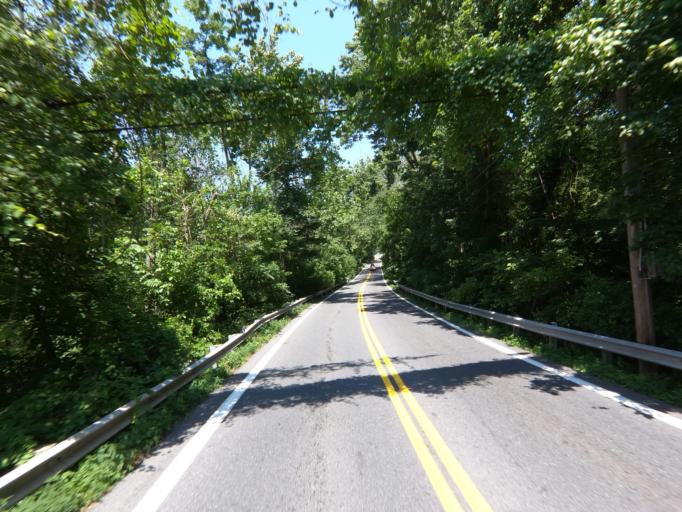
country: US
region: Maryland
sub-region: Frederick County
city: Green Valley
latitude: 39.2779
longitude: -77.3145
